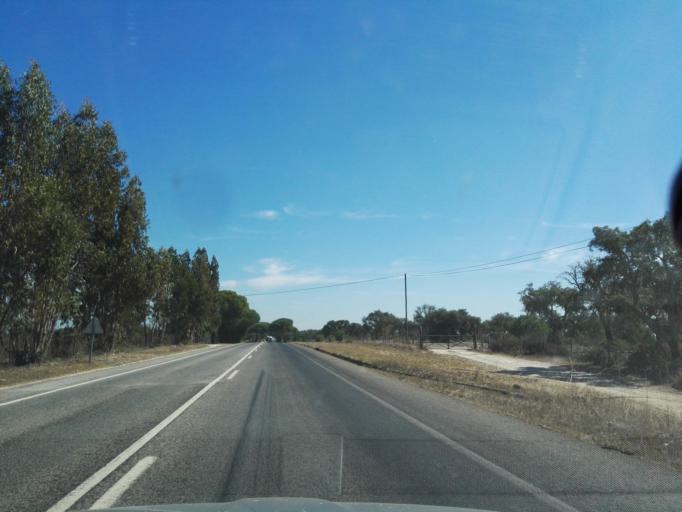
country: PT
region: Santarem
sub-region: Benavente
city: Poceirao
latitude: 38.8456
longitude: -8.7599
